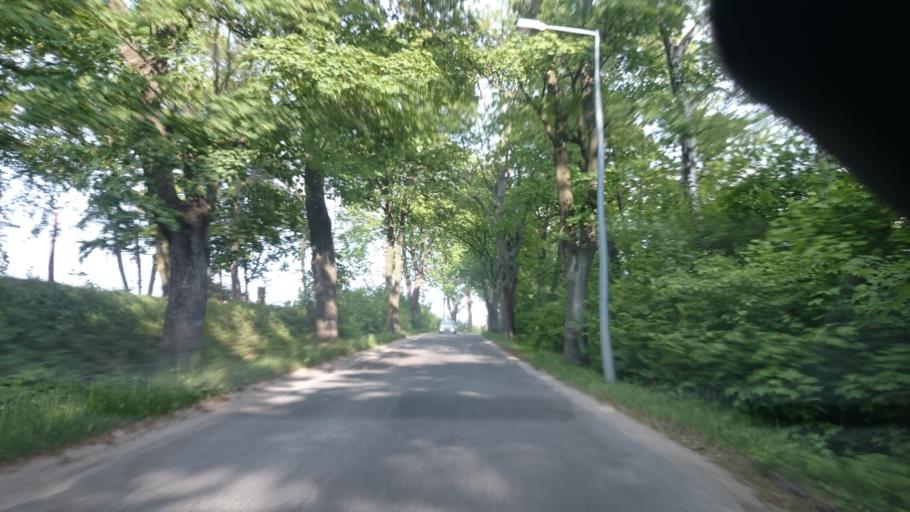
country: PL
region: Lower Silesian Voivodeship
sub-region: Powiat klodzki
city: Bystrzyca Klodzka
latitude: 50.2930
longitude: 16.6560
